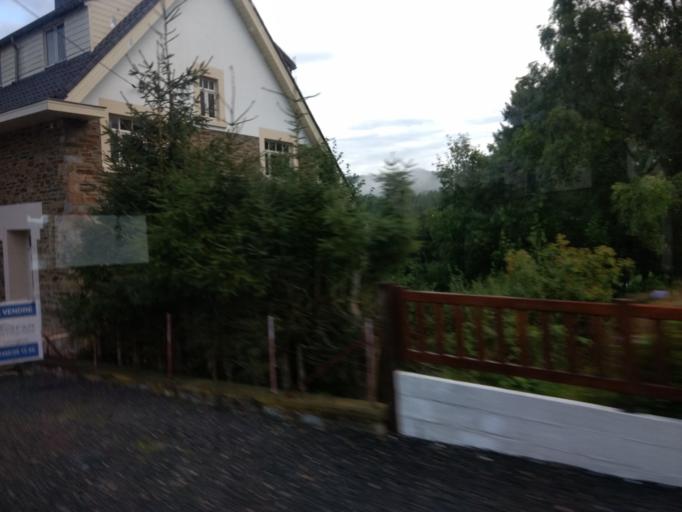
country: BE
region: Wallonia
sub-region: Province du Luxembourg
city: La Roche-en-Ardenne
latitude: 50.1801
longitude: 5.6619
